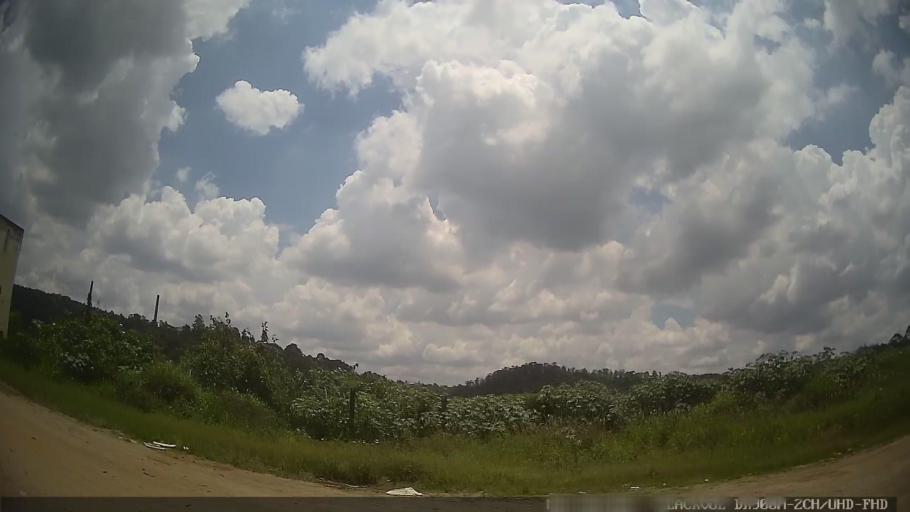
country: BR
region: Sao Paulo
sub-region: Ferraz De Vasconcelos
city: Ferraz de Vasconcelos
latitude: -23.5883
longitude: -46.3608
